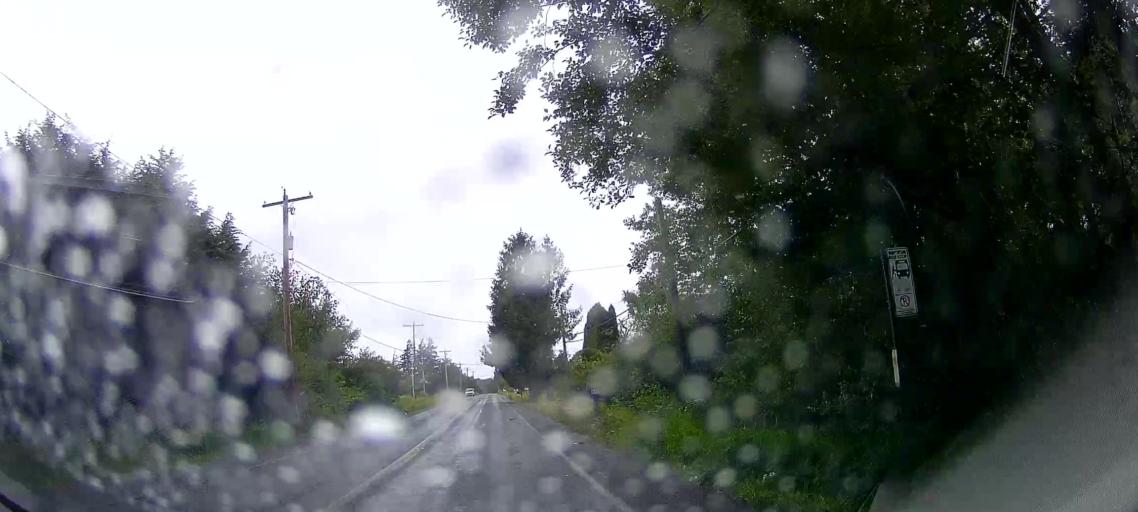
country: US
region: Washington
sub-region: Whatcom County
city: Marietta-Alderwood
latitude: 48.7832
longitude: -122.5619
